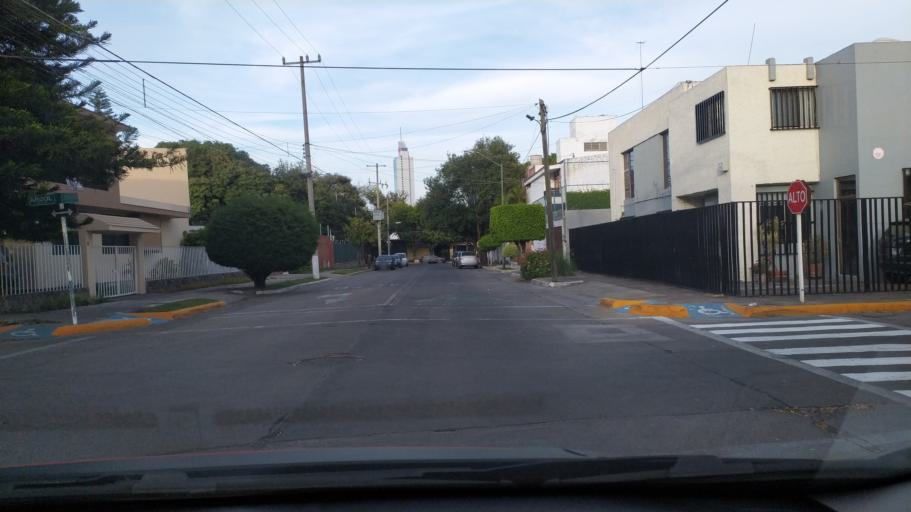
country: MX
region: Jalisco
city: Guadalajara
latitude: 20.6585
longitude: -103.4003
